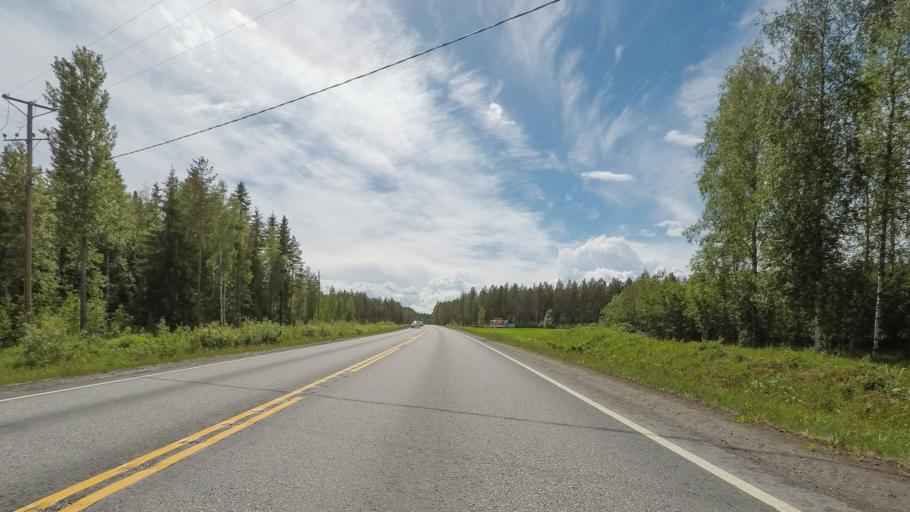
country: FI
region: Central Finland
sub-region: Jyvaeskylae
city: Hankasalmi
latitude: 62.3771
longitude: 26.5902
